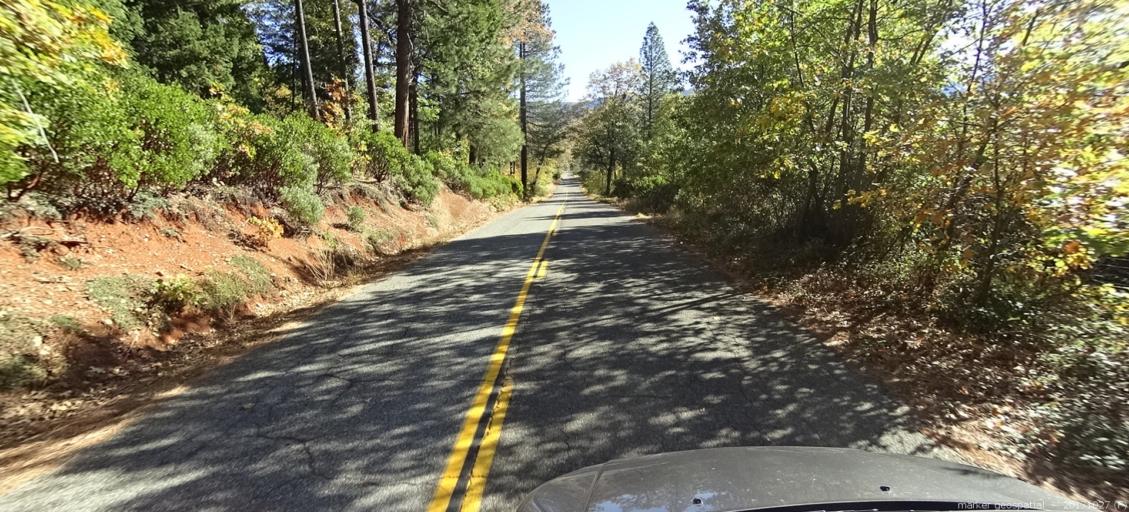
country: US
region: California
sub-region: Shasta County
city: Burney
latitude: 40.8261
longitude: -121.9471
